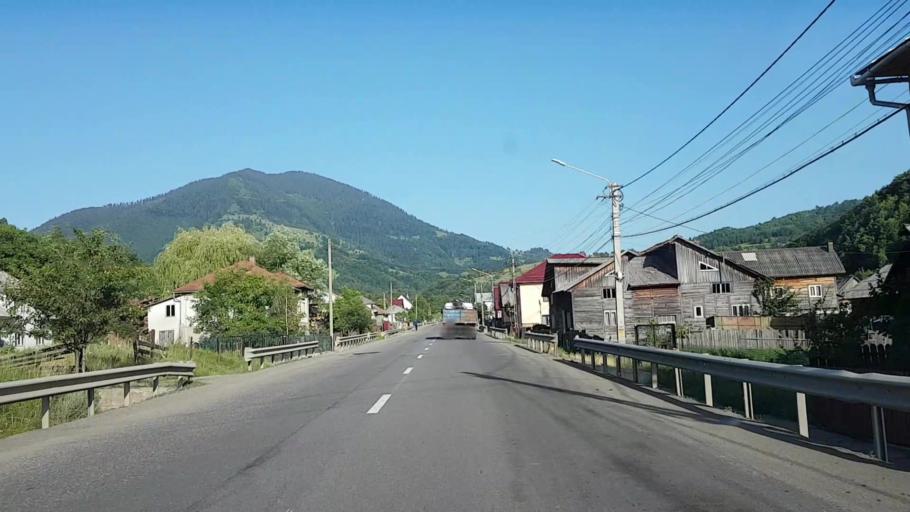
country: RO
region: Bistrita-Nasaud
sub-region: Comuna Tiha Bargaului
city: Tureac
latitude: 47.2140
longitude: 24.8486
